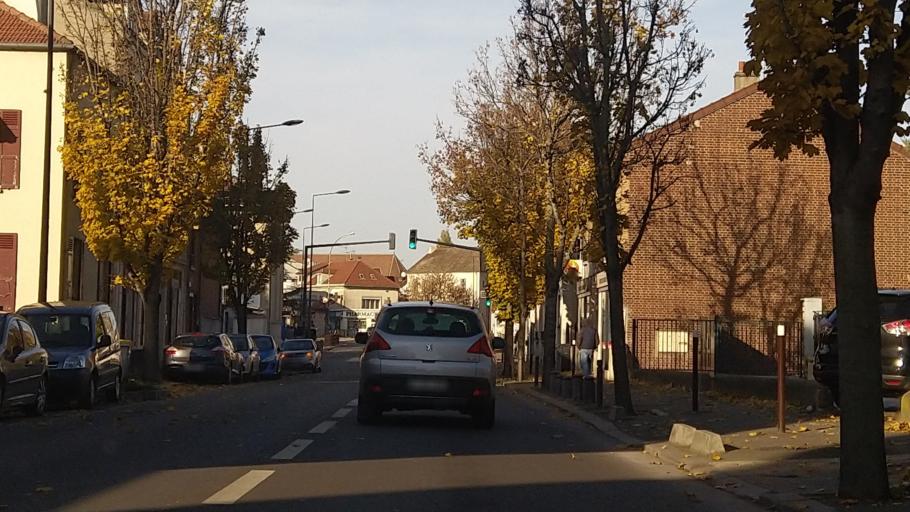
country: FR
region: Ile-de-France
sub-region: Departement de Seine-Saint-Denis
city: Stains
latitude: 48.9541
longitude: 2.3840
